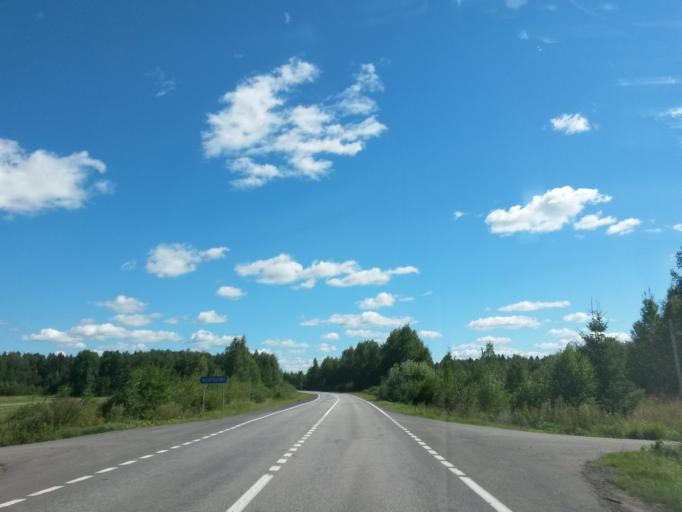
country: RU
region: Jaroslavl
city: Konstantinovskiy
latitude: 57.8093
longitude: 39.7370
